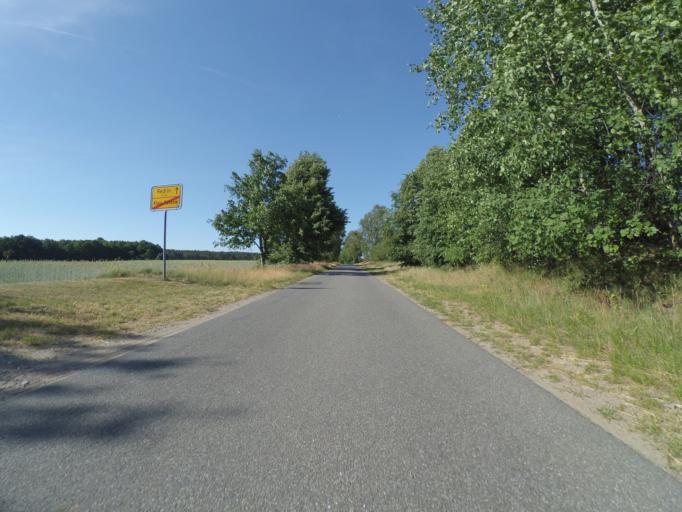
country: DE
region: Mecklenburg-Vorpommern
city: Lubz
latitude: 53.3728
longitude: 12.0339
